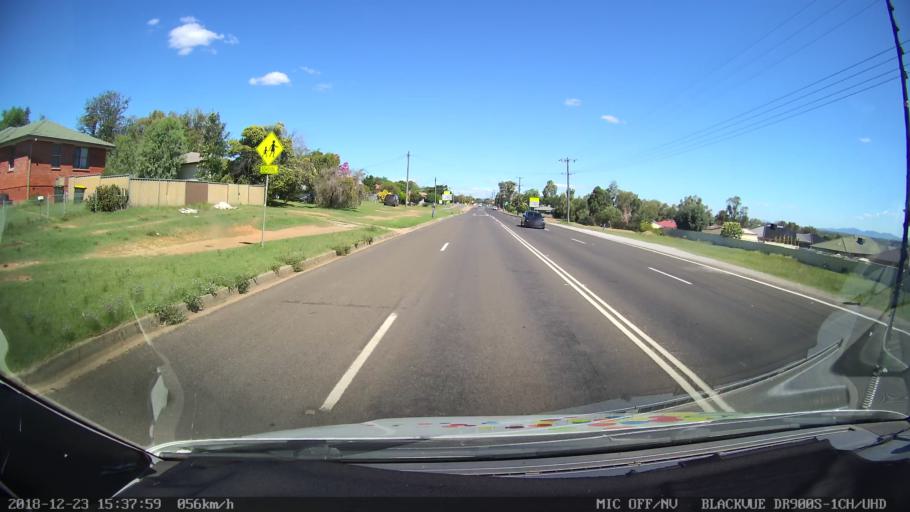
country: AU
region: New South Wales
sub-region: Tamworth Municipality
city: Tamworth
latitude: -31.0560
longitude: 150.8935
